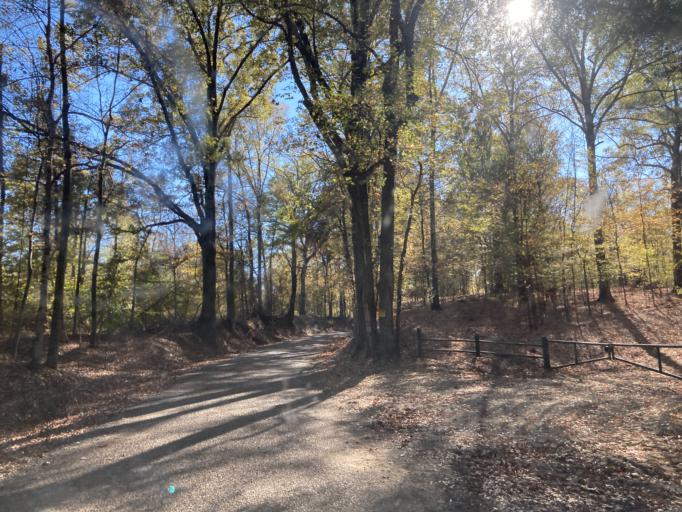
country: US
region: Mississippi
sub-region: Yazoo County
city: Yazoo City
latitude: 32.7788
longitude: -90.4069
